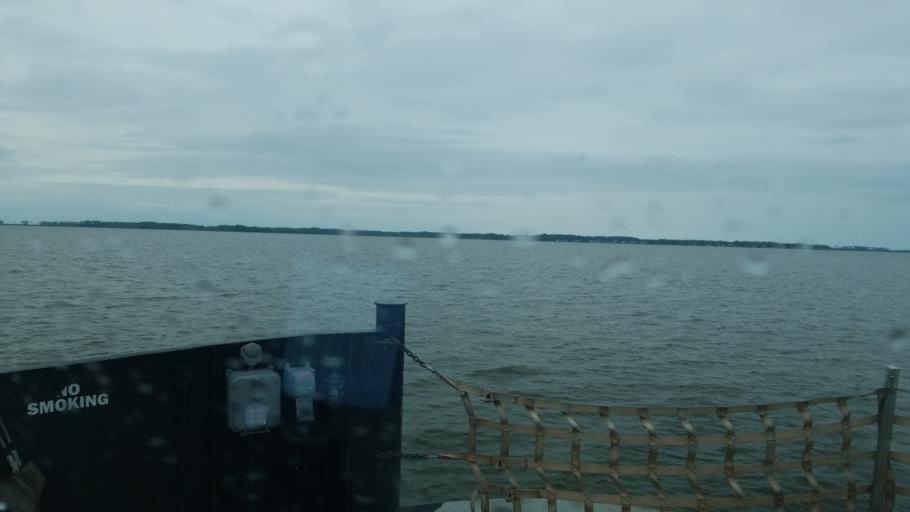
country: US
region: North Carolina
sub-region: Currituck County
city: Currituck
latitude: 36.4705
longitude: -75.9538
